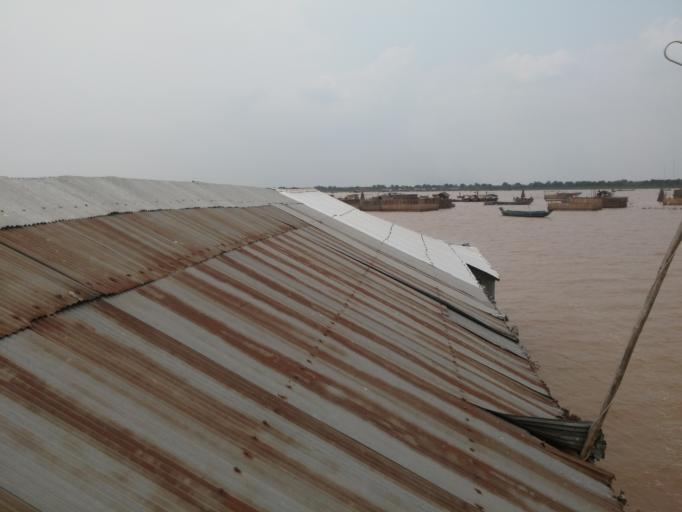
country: KH
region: Siem Reap
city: Siem Reap
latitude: 13.1891
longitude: 103.9677
